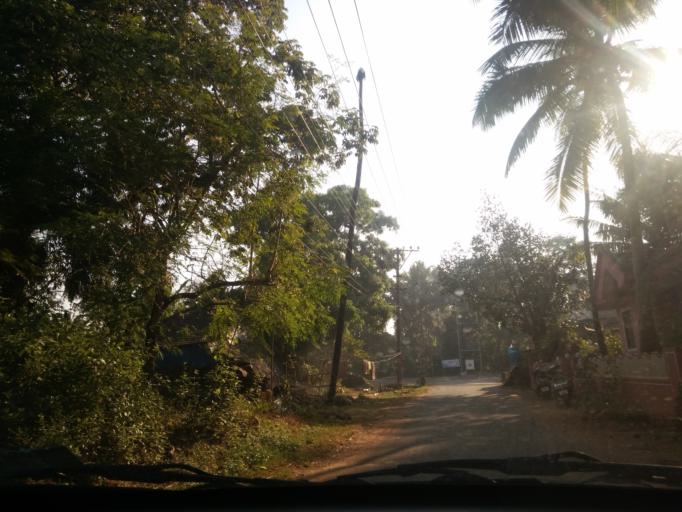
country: IN
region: Goa
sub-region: South Goa
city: Chinchinim
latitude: 15.2039
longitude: 73.9877
